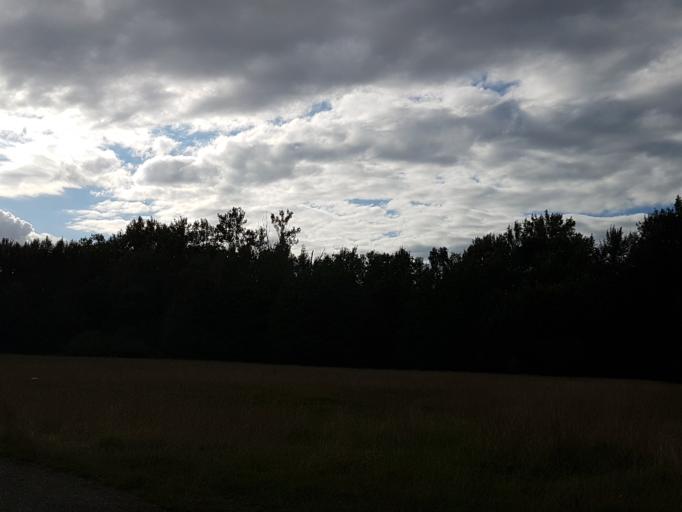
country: BE
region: Flanders
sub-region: Provincie Vlaams-Brabant
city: Kampenhout
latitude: 50.9163
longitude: 4.5847
